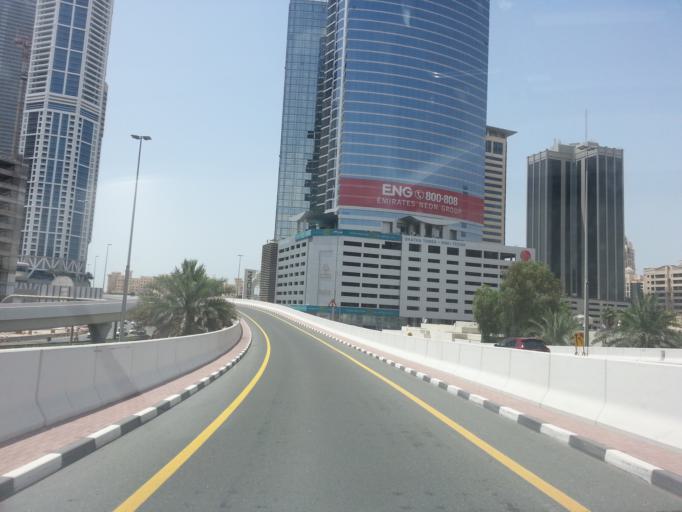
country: AE
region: Dubai
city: Dubai
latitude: 25.0877
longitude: 55.1538
